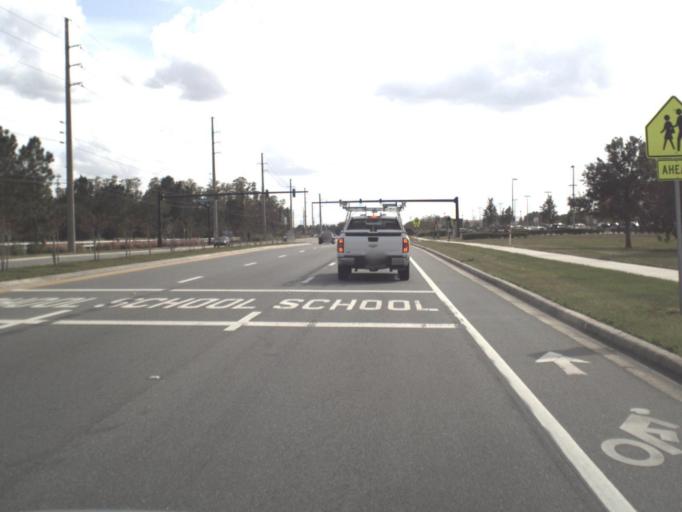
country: US
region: Florida
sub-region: Osceola County
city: Buenaventura Lakes
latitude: 28.3693
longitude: -81.2446
